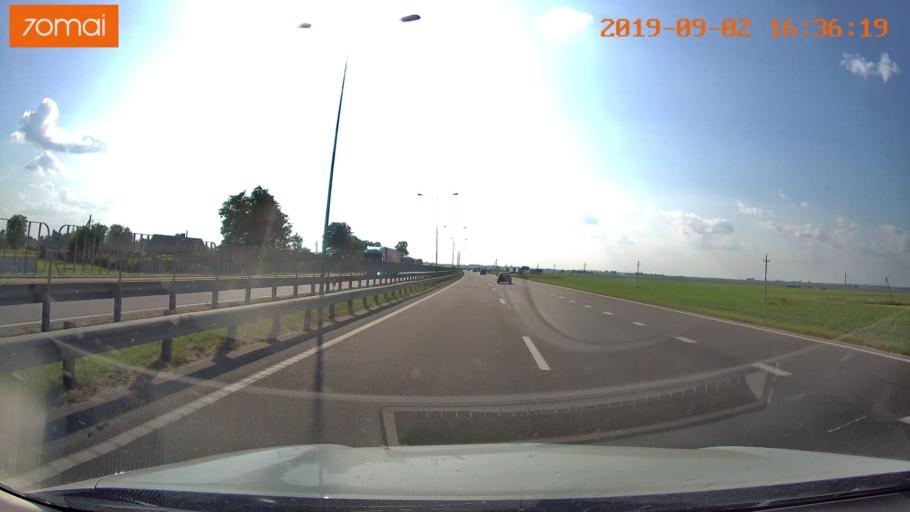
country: BY
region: Minsk
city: Smilavichy
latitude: 53.7598
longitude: 27.9803
